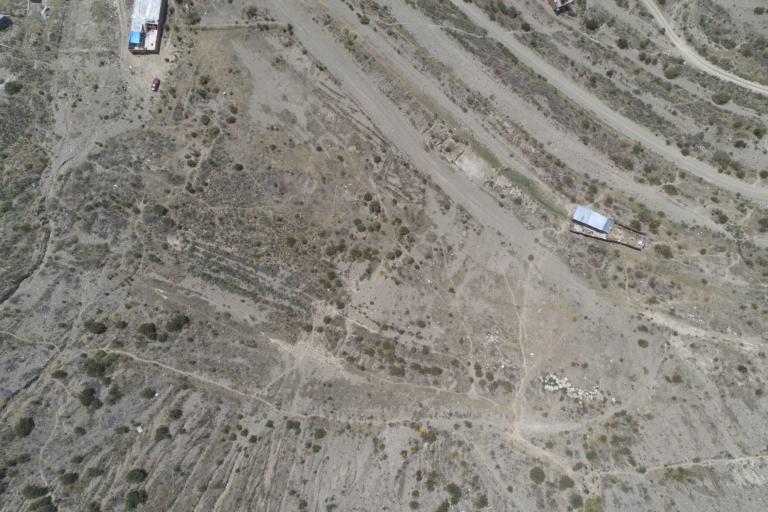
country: BO
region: La Paz
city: La Paz
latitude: -16.5027
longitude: -68.0997
